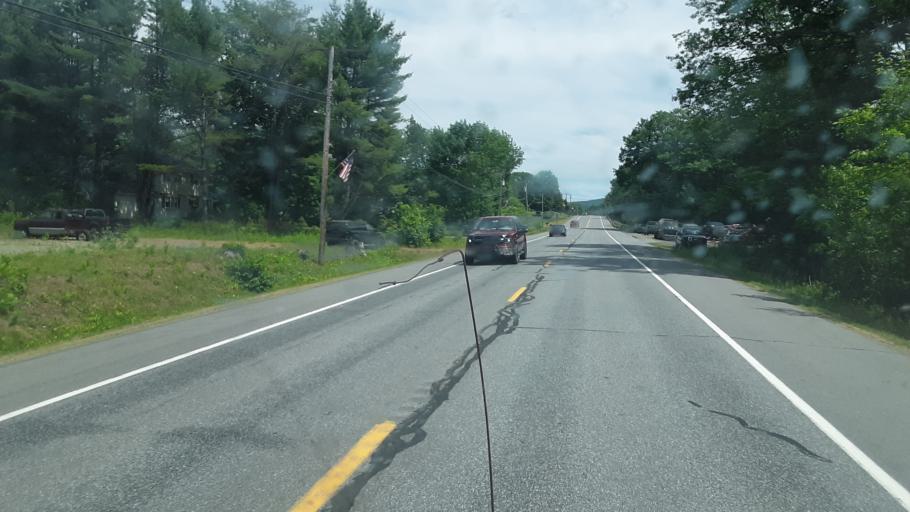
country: US
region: Maine
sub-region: Franklin County
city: New Sharon
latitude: 44.6434
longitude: -70.0219
